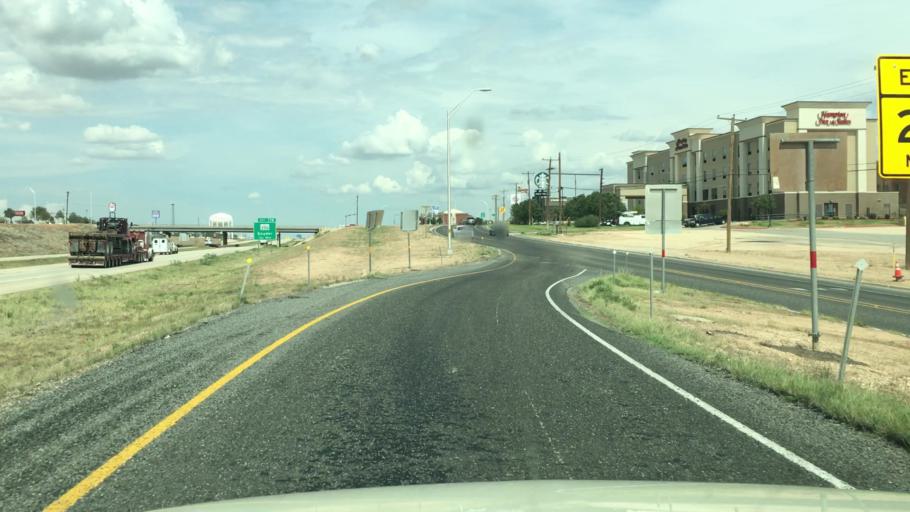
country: US
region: Texas
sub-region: Howard County
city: Big Spring
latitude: 32.2625
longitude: -101.4939
